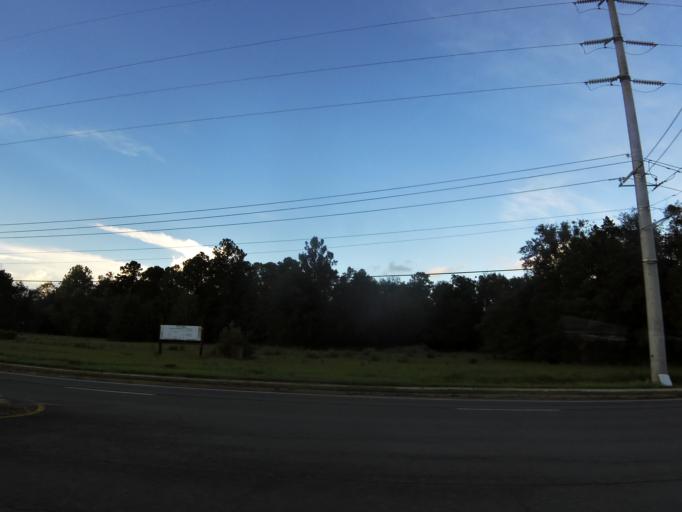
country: US
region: Georgia
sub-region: Camden County
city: St Marys
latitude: 30.7539
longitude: -81.5885
